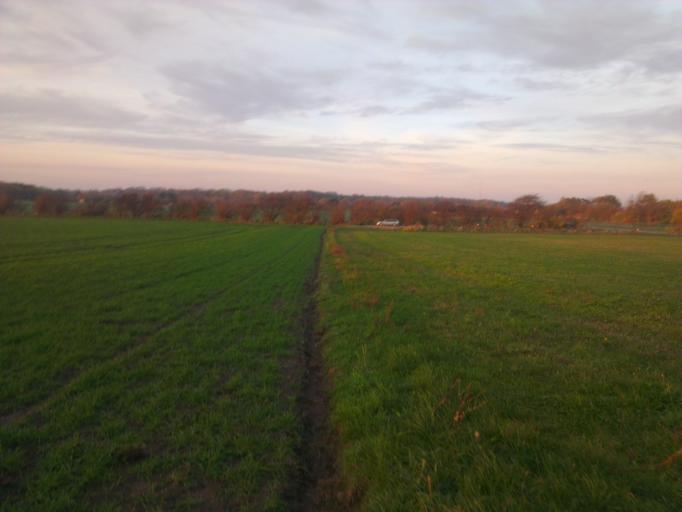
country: DK
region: Capital Region
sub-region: Frederikssund Kommune
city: Jaegerspris
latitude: 55.8470
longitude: 11.9833
